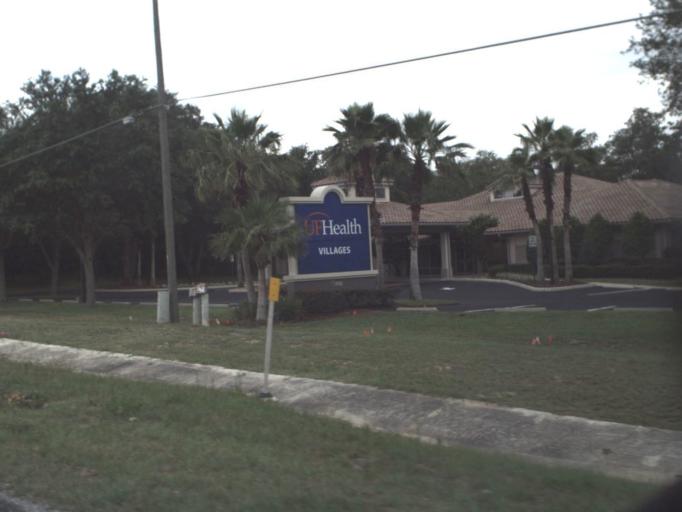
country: US
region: Florida
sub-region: Sumter County
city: The Villages
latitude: 28.9744
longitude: -81.9800
